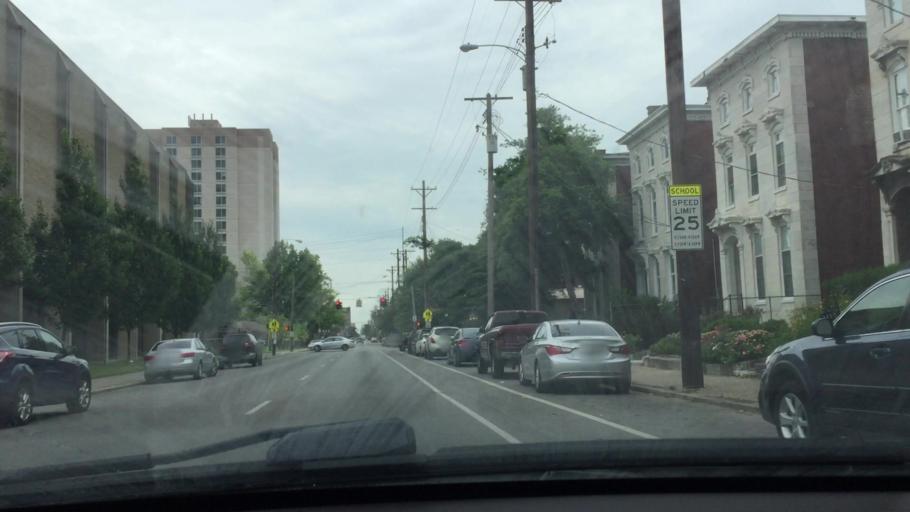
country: US
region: Kentucky
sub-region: Jefferson County
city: Louisville
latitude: 38.2362
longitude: -85.7568
